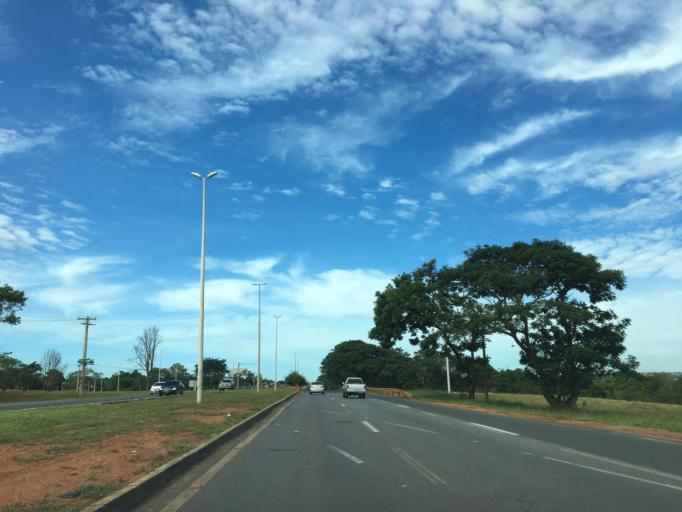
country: BR
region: Federal District
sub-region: Brasilia
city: Brasilia
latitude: -15.8651
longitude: -47.9415
